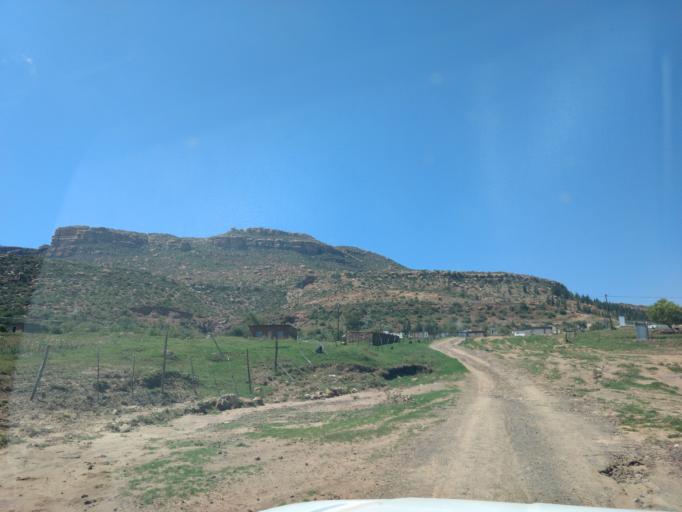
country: LS
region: Maseru
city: Maseru
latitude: -29.4023
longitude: 27.4342
